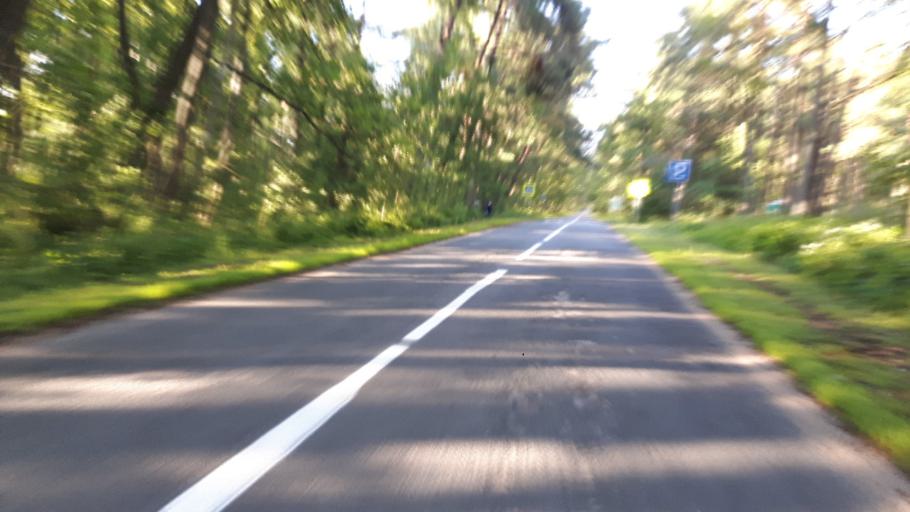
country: LT
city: Nida
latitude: 55.2480
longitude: 20.9235
